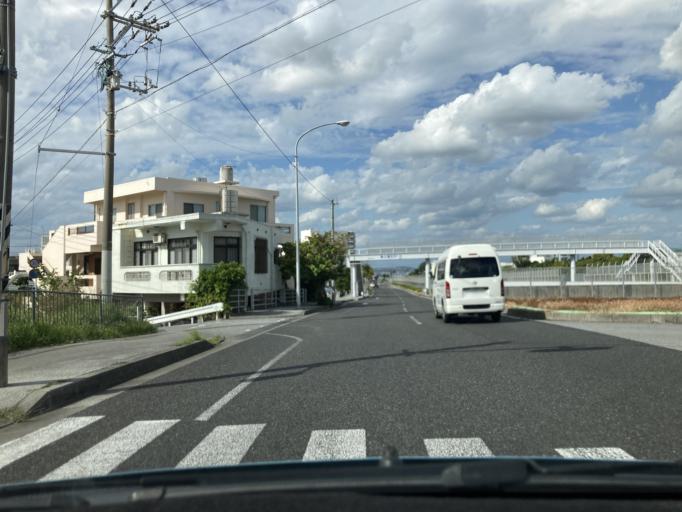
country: JP
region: Okinawa
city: Okinawa
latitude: 26.3229
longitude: 127.7887
